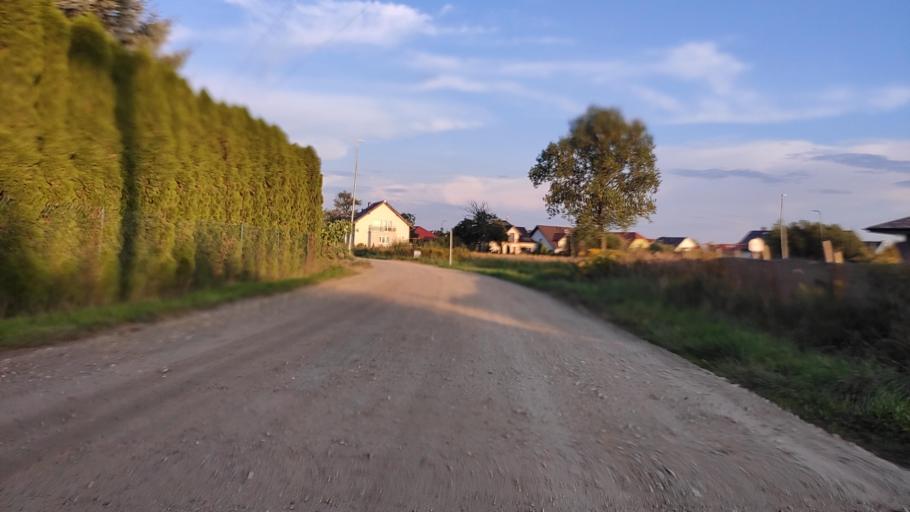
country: PL
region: Greater Poland Voivodeship
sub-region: Powiat poznanski
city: Kleszczewo
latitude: 52.3906
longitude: 17.1591
